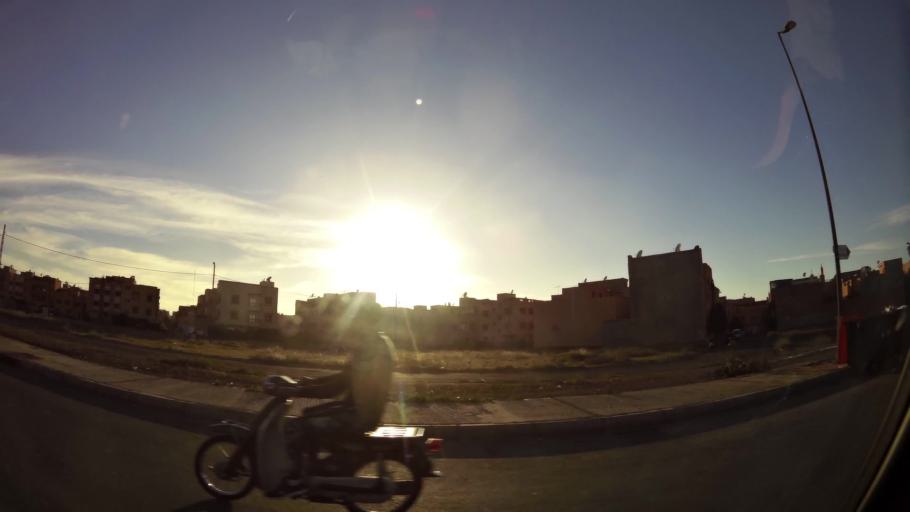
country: MA
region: Marrakech-Tensift-Al Haouz
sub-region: Marrakech
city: Marrakesh
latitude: 31.6191
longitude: -8.0446
